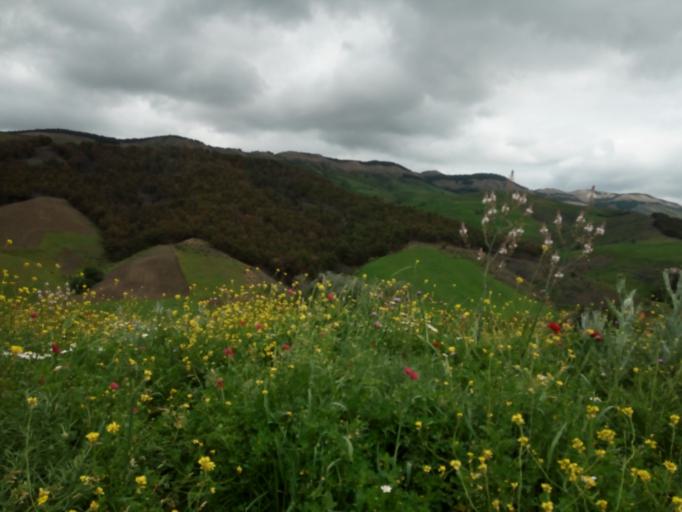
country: DZ
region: Setif
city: El Eulma
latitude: 36.3234
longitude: 5.7341
